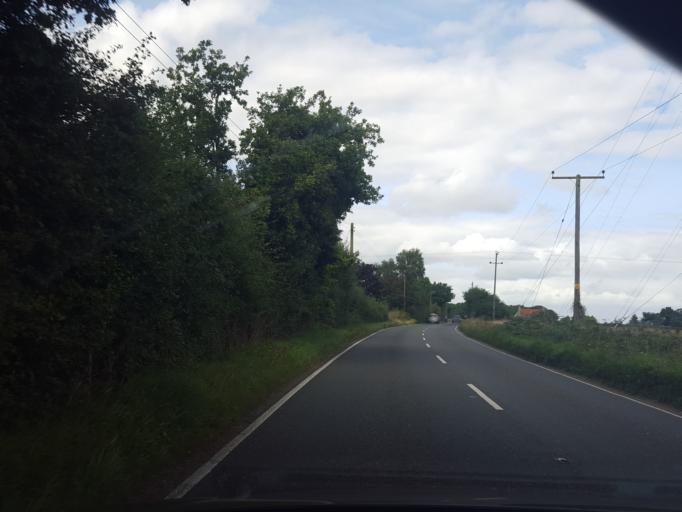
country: GB
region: England
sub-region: Essex
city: Mistley
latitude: 51.9221
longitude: 1.0845
